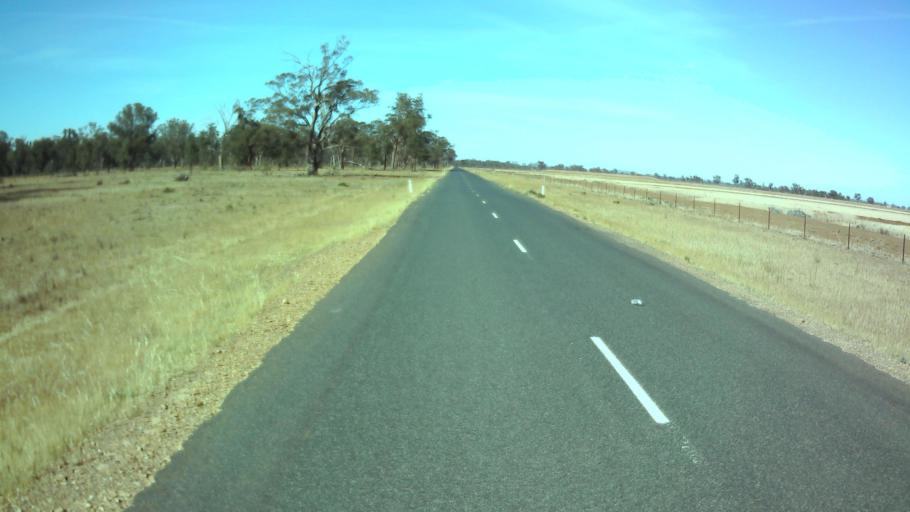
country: AU
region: New South Wales
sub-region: Weddin
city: Grenfell
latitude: -34.1213
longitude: 147.8106
